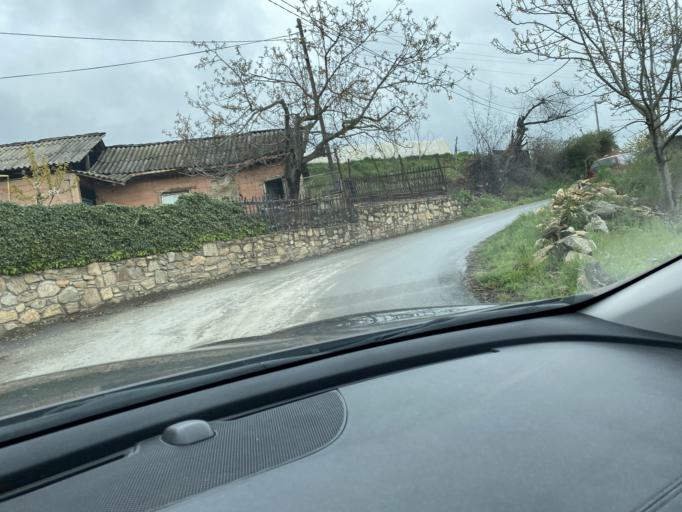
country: MK
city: Creshevo
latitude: 42.0530
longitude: 21.5196
